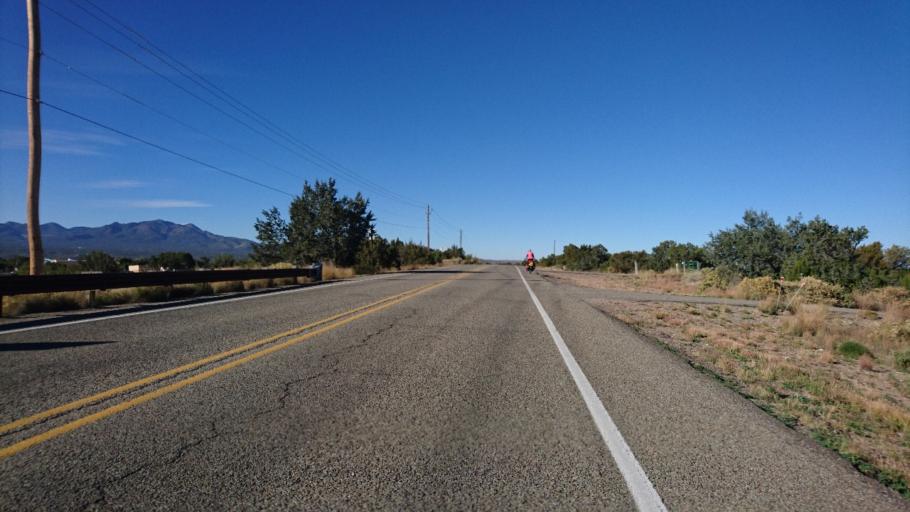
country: US
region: New Mexico
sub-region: Santa Fe County
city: La Cienega
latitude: 35.4525
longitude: -106.0724
